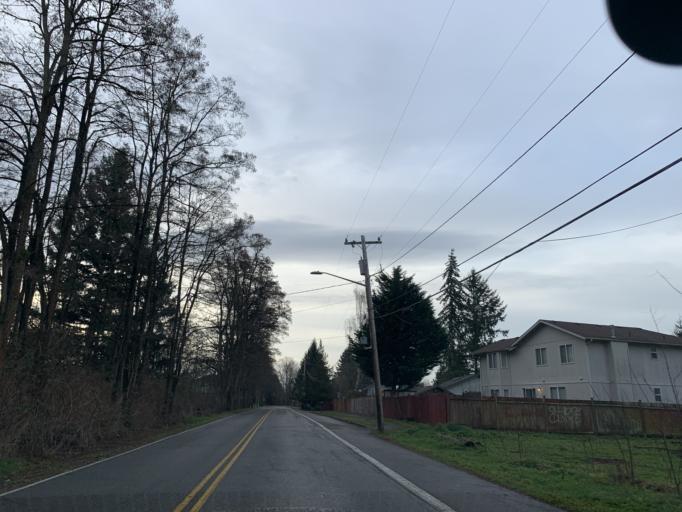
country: US
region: Washington
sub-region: Snohomish County
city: Marysville
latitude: 48.0832
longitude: -122.1565
